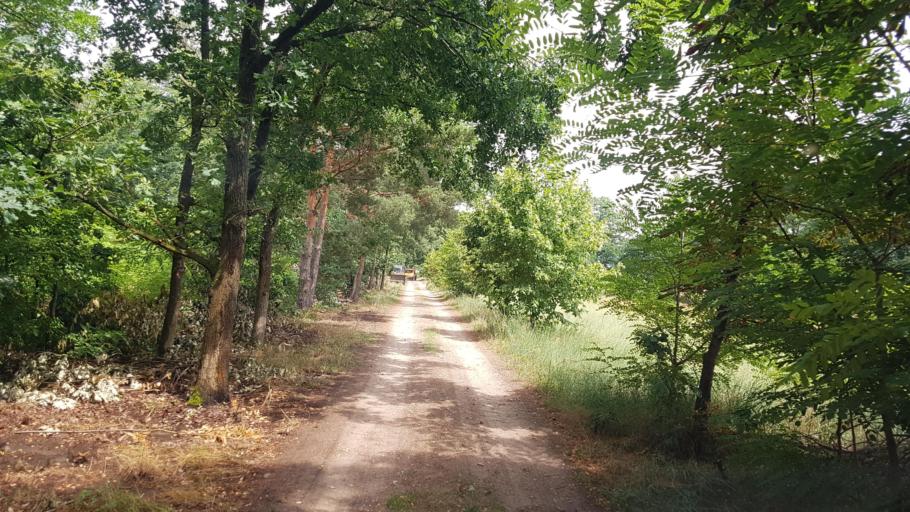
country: DE
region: Brandenburg
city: Trebbin
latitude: 52.2437
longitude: 13.1703
